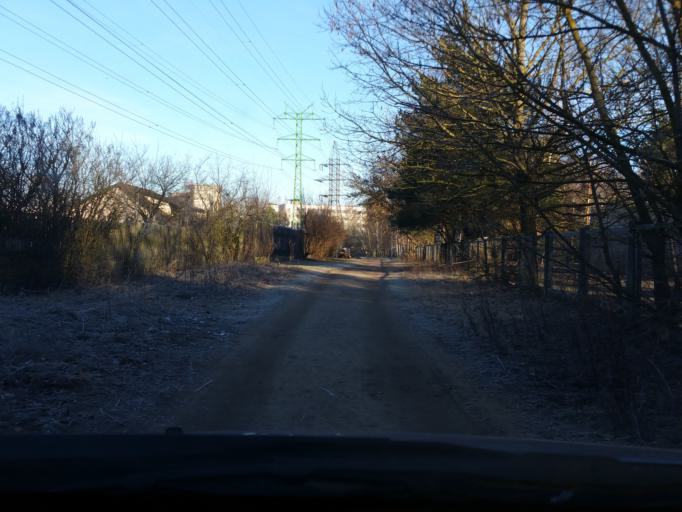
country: LV
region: Riga
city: Jaunciems
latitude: 56.9737
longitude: 24.1955
